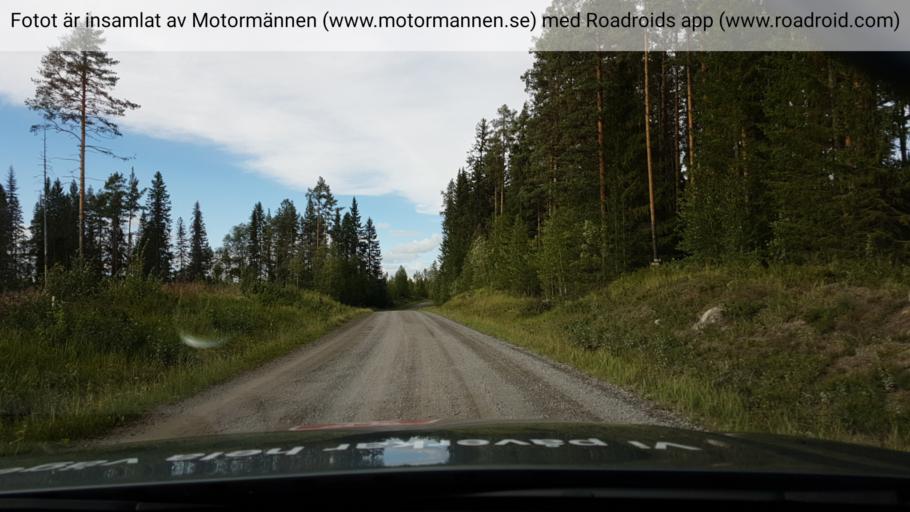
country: SE
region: Jaemtland
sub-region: Braecke Kommun
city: Braecke
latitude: 63.2420
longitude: 15.3699
